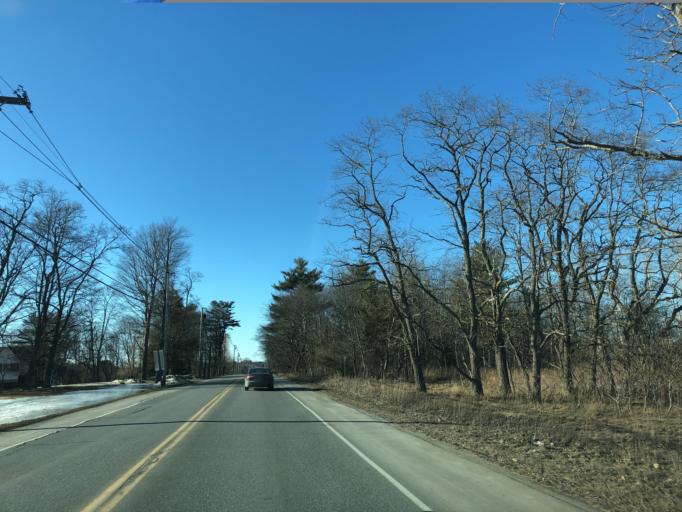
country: US
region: Maine
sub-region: Penobscot County
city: Bangor
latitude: 44.8465
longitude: -68.8013
